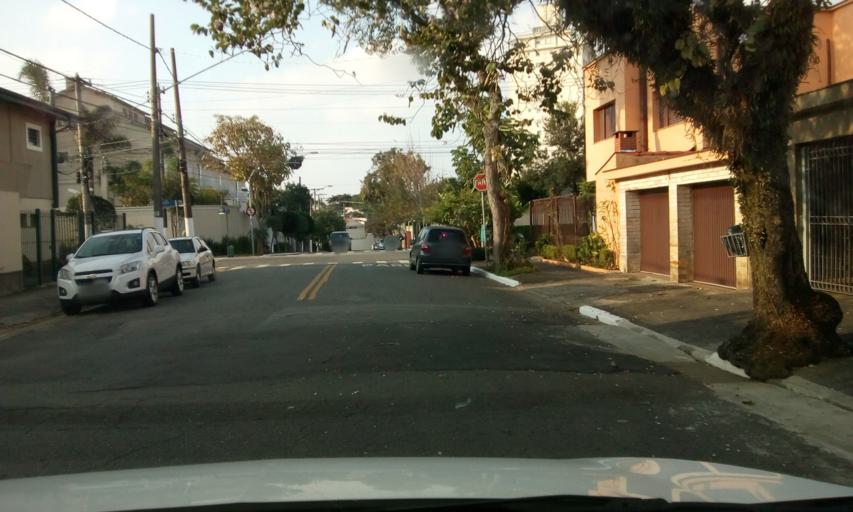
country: BR
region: Sao Paulo
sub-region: Sao Paulo
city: Sao Paulo
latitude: -23.6185
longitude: -46.6522
